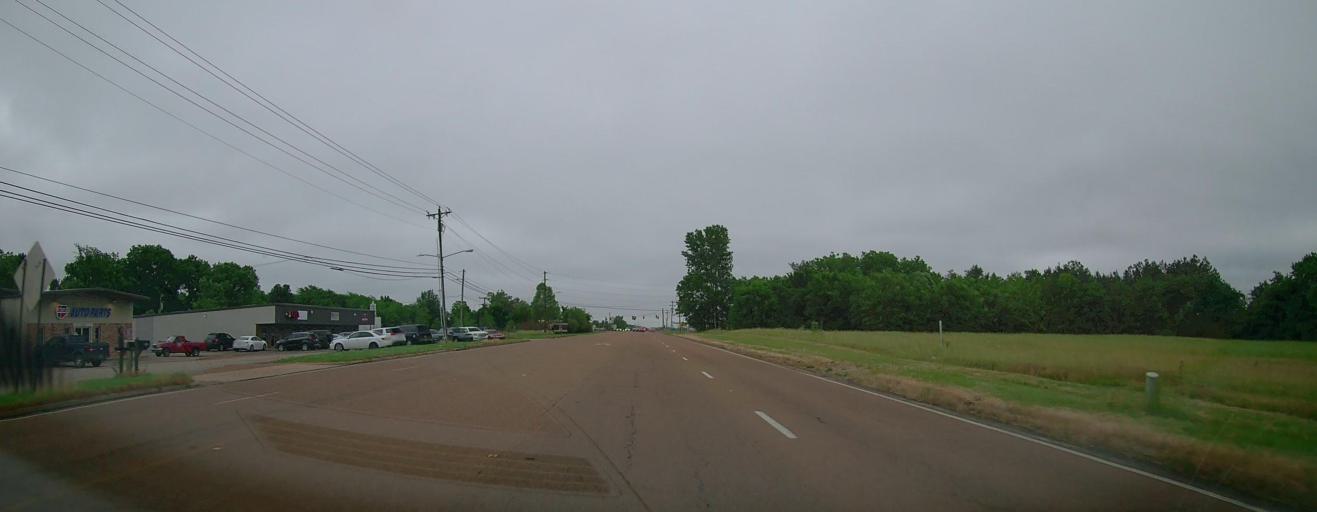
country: US
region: Mississippi
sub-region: De Soto County
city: Olive Branch
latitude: 34.9358
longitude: -89.7950
